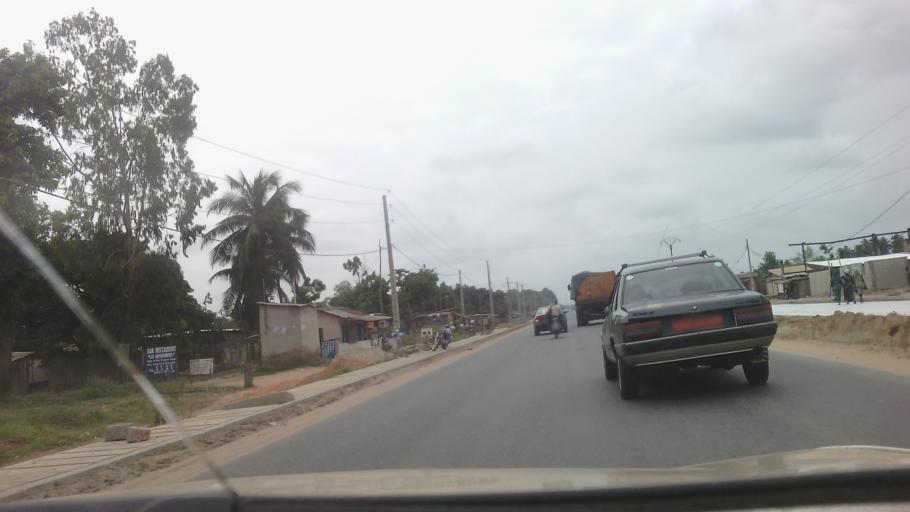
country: BJ
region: Atlantique
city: Hevie
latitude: 6.3834
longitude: 2.1873
